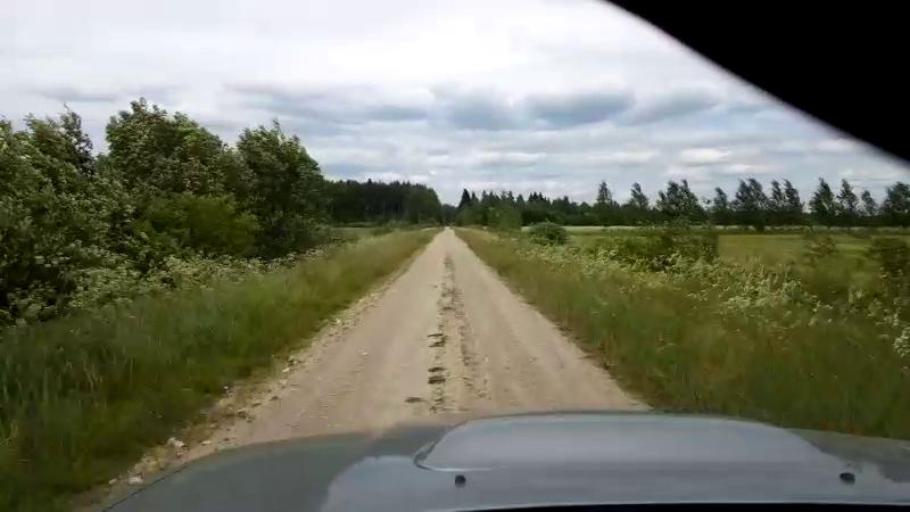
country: EE
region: Paernumaa
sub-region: Sauga vald
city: Sauga
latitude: 58.4989
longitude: 24.5809
